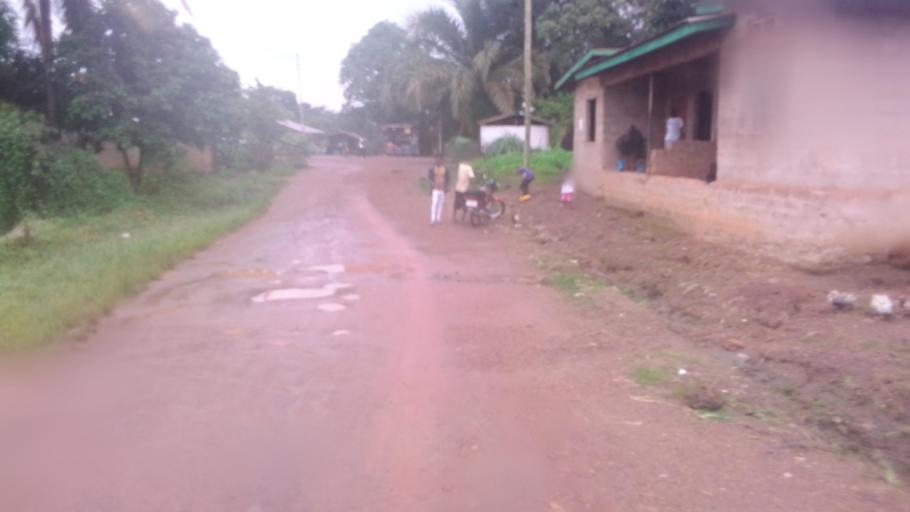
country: SL
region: Eastern Province
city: Kenema
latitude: 7.8875
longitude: -11.1757
